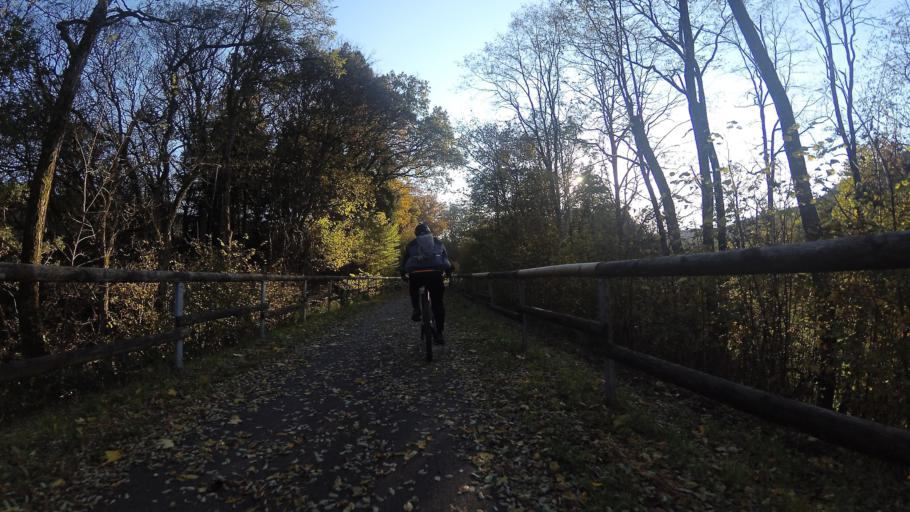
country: DE
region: Rheinland-Pfalz
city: Heddert
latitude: 49.6438
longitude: 6.7281
